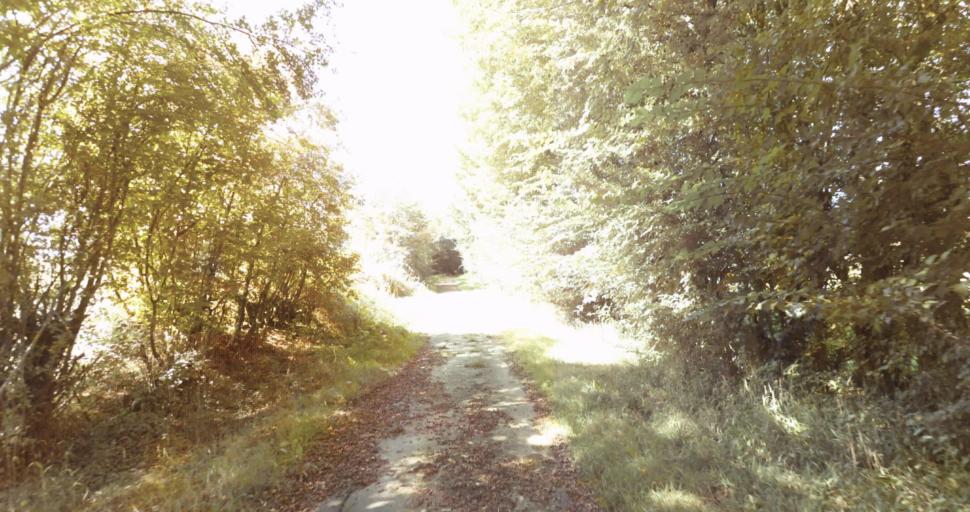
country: FR
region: Lower Normandy
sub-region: Departement de l'Orne
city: Gace
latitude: 48.7712
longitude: 0.2992
